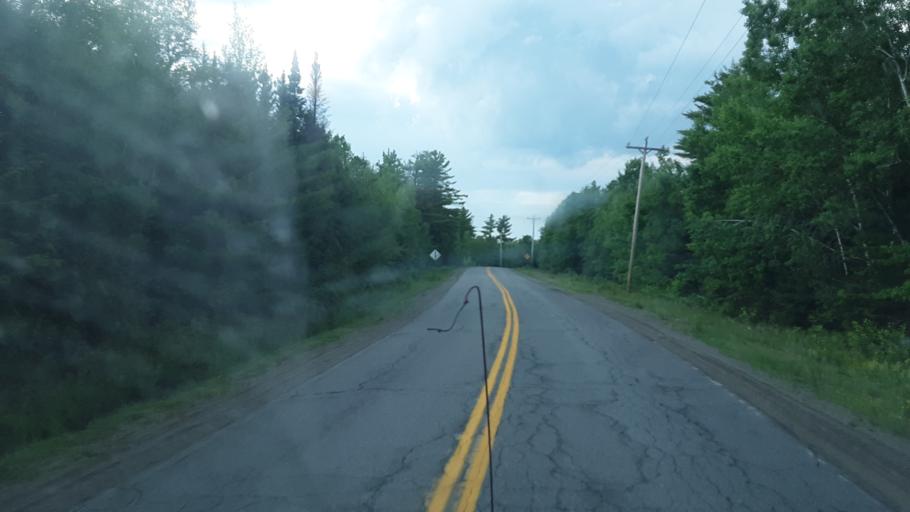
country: US
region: Maine
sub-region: Washington County
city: Calais
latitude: 45.1208
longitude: -67.4991
